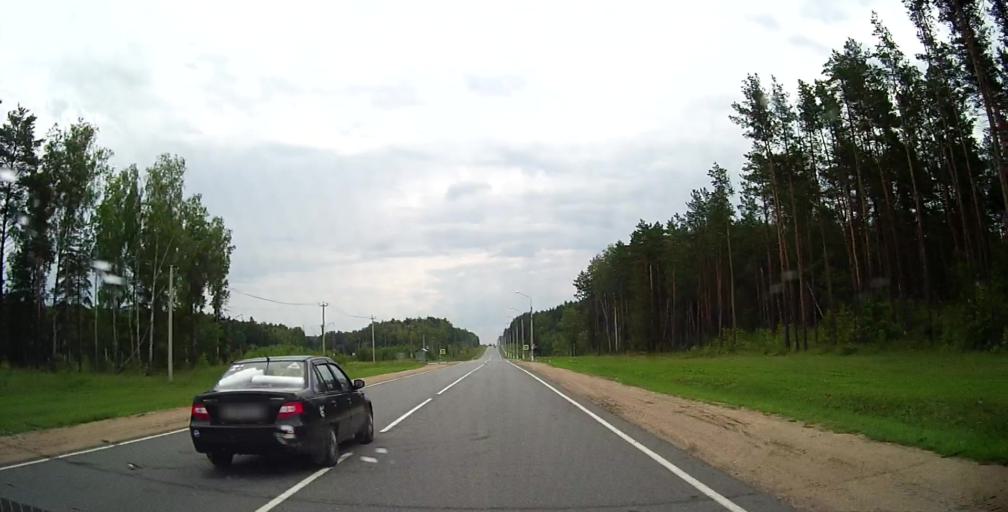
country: RU
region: Smolensk
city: Katyn'
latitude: 54.7712
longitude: 31.7647
